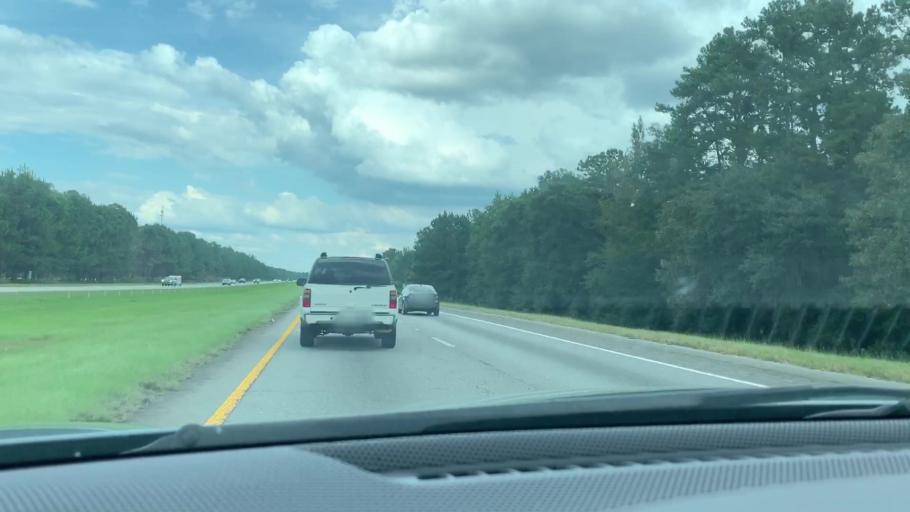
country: US
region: South Carolina
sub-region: Hampton County
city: Yemassee
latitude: 32.6051
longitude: -80.8980
